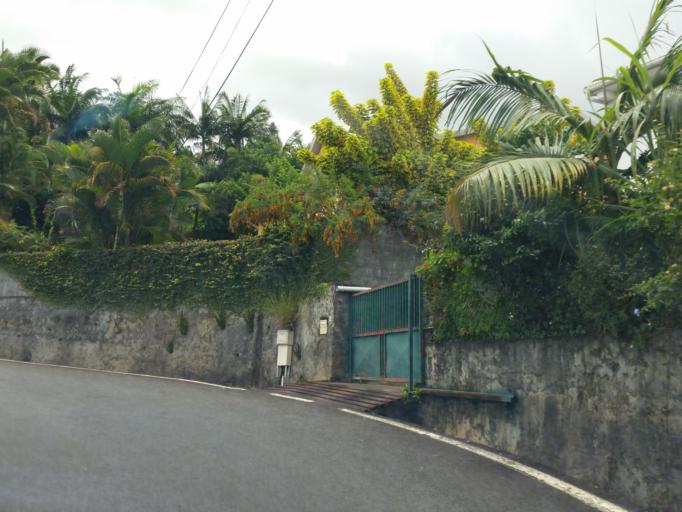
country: RE
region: Reunion
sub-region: Reunion
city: Sainte-Marie
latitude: -20.9360
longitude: 55.5417
